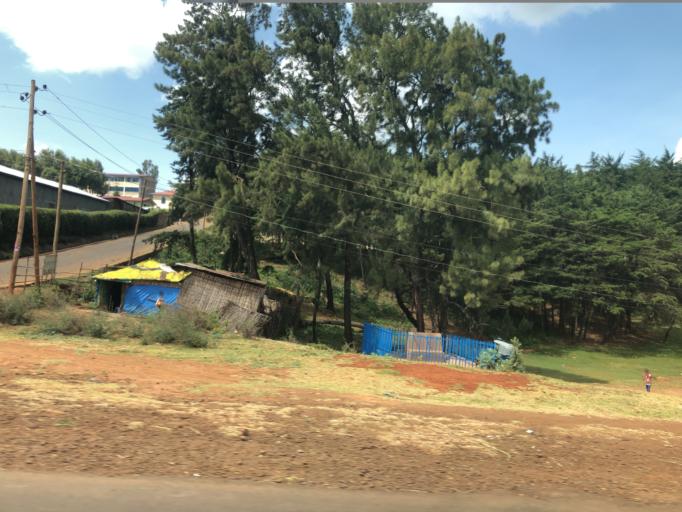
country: ET
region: Southern Nations, Nationalities, and People's Region
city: Boditi
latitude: 6.8724
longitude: 37.7710
